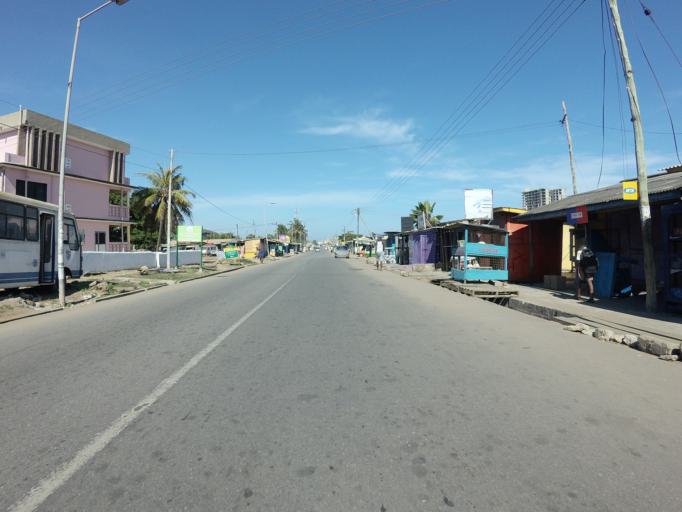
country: GH
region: Greater Accra
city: Accra
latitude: 5.5618
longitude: -0.1512
